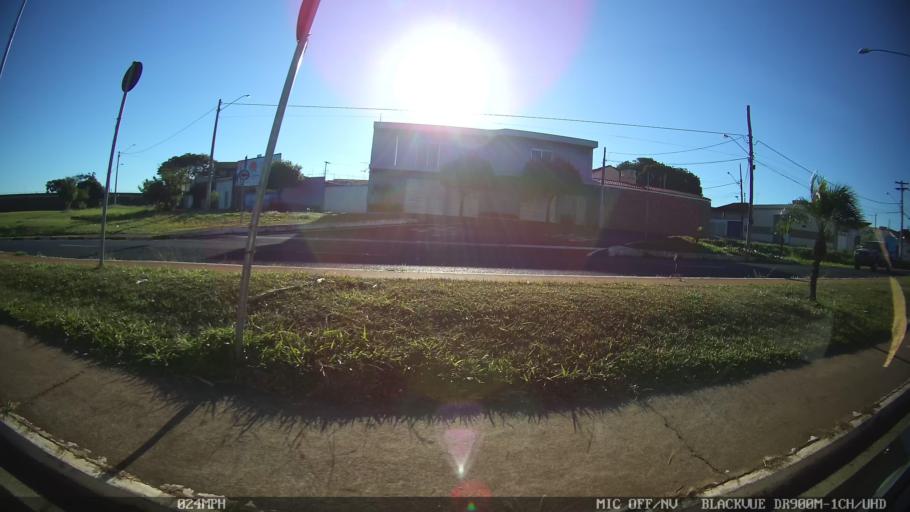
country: BR
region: Sao Paulo
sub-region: Franca
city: Franca
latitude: -20.5727
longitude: -47.3910
